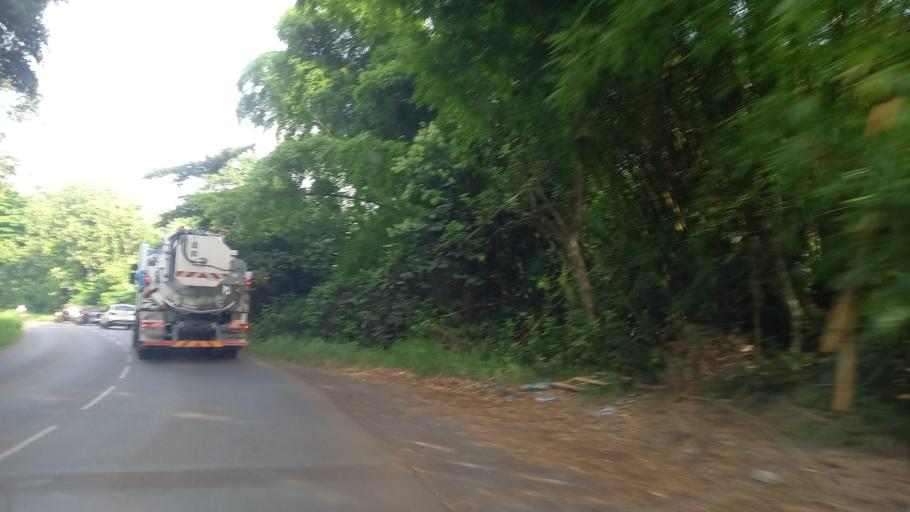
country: YT
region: Chiconi
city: Chiconi
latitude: -12.8078
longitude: 45.1271
